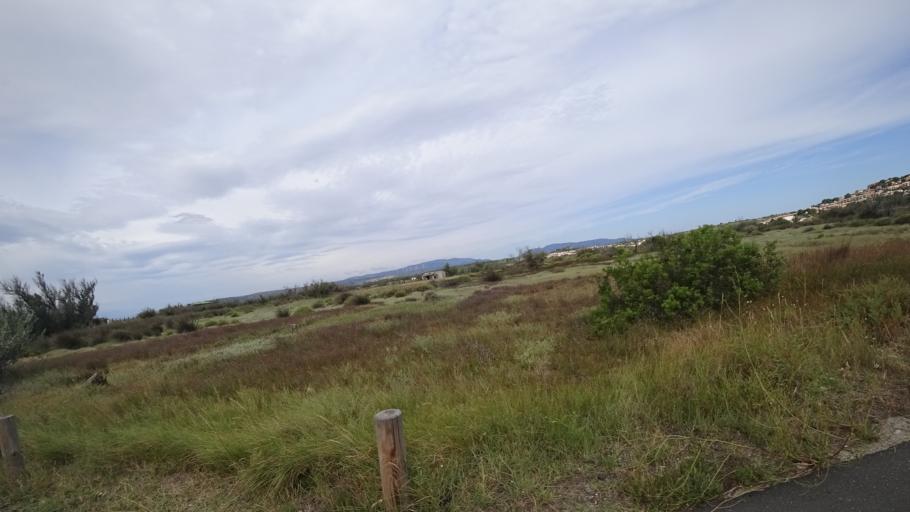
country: FR
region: Languedoc-Roussillon
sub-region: Departement de l'Aude
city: Leucate
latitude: 42.8976
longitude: 3.0519
